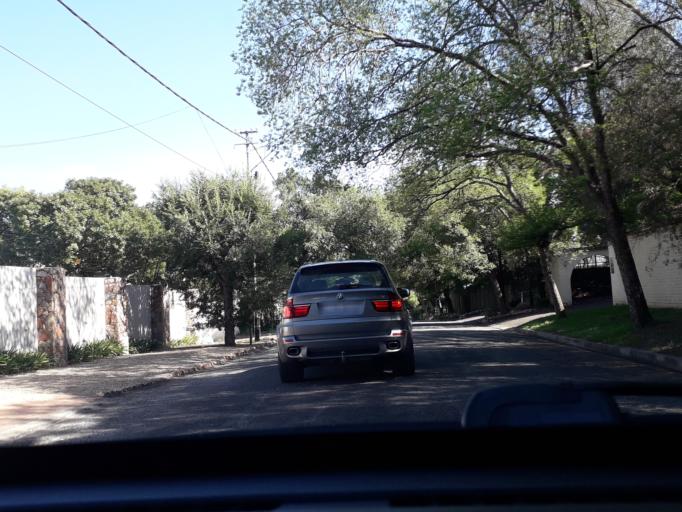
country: ZA
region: Gauteng
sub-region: City of Johannesburg Metropolitan Municipality
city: Johannesburg
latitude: -26.1274
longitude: 28.0304
